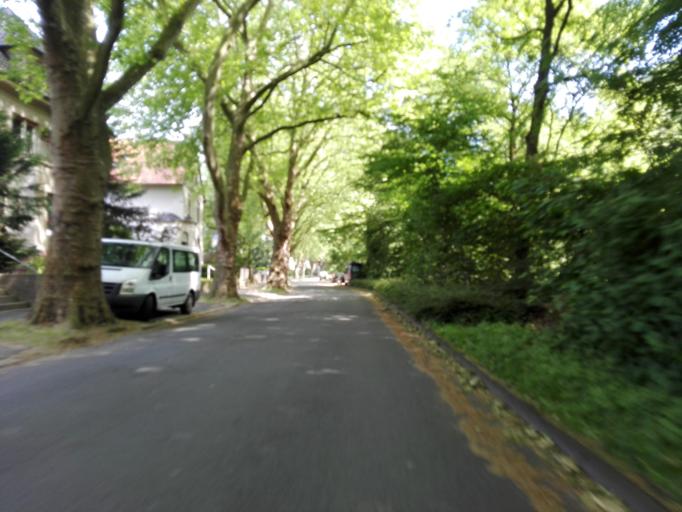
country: DE
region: North Rhine-Westphalia
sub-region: Regierungsbezirk Arnsberg
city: Unna
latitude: 51.5282
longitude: 7.6883
